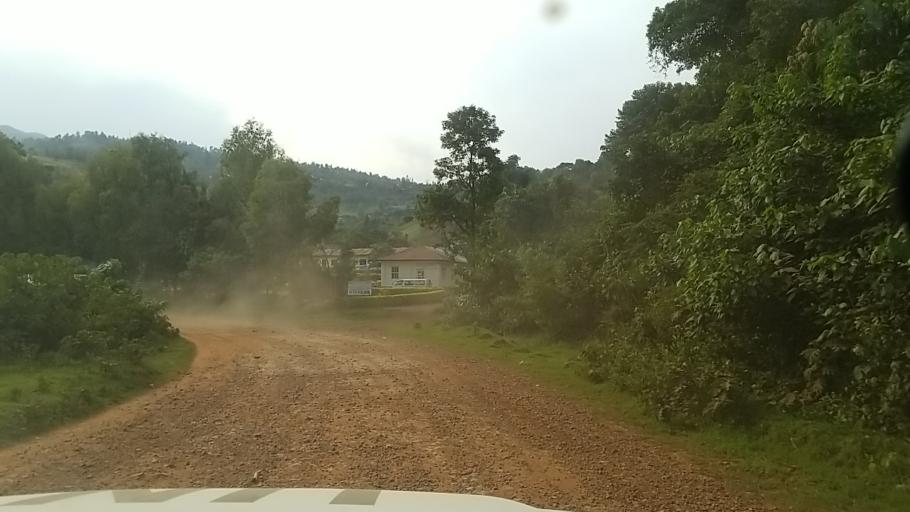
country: RW
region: Western Province
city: Cyangugu
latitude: -2.1051
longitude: 28.9105
